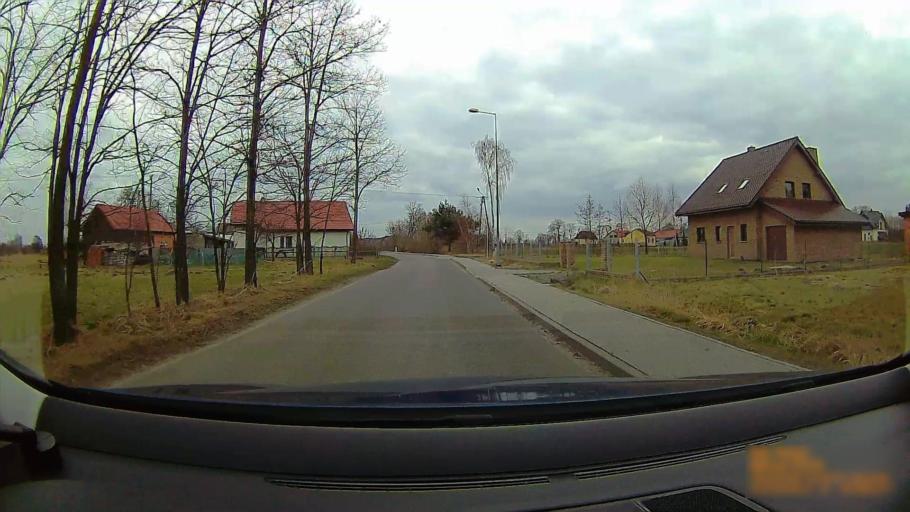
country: PL
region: Greater Poland Voivodeship
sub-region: Powiat koninski
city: Rychwal
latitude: 52.0794
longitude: 18.1348
